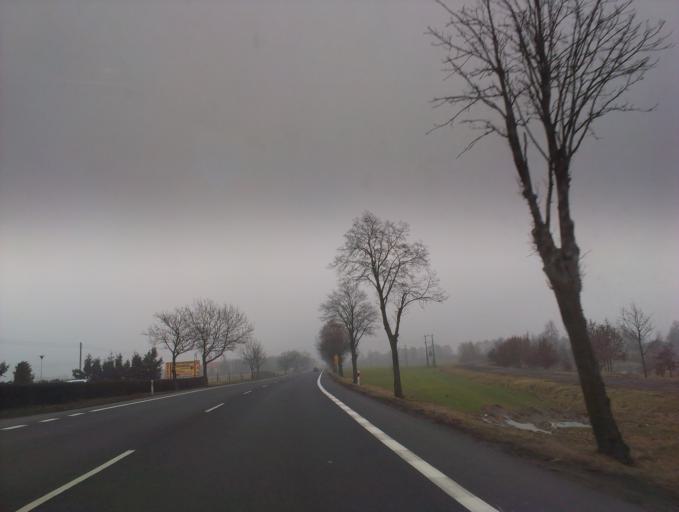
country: PL
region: Greater Poland Voivodeship
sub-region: Powiat pilski
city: Ujscie
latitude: 53.0429
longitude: 16.7609
